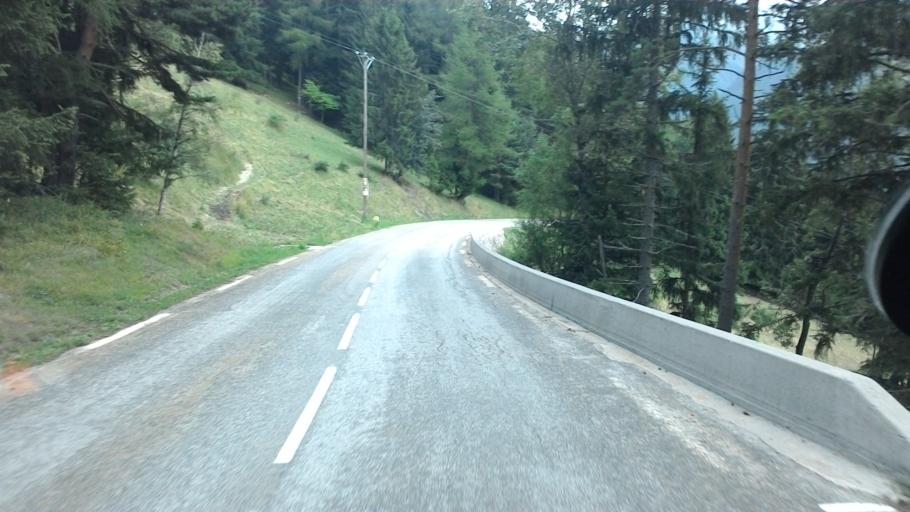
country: FR
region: Rhone-Alpes
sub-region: Departement de la Savoie
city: Seez
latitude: 45.6270
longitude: 6.8203
